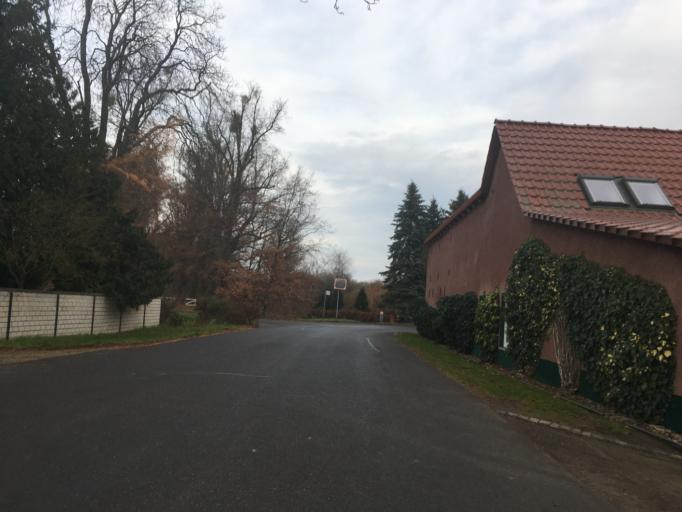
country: DE
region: Brandenburg
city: Seelow
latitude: 52.5689
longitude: 14.3476
